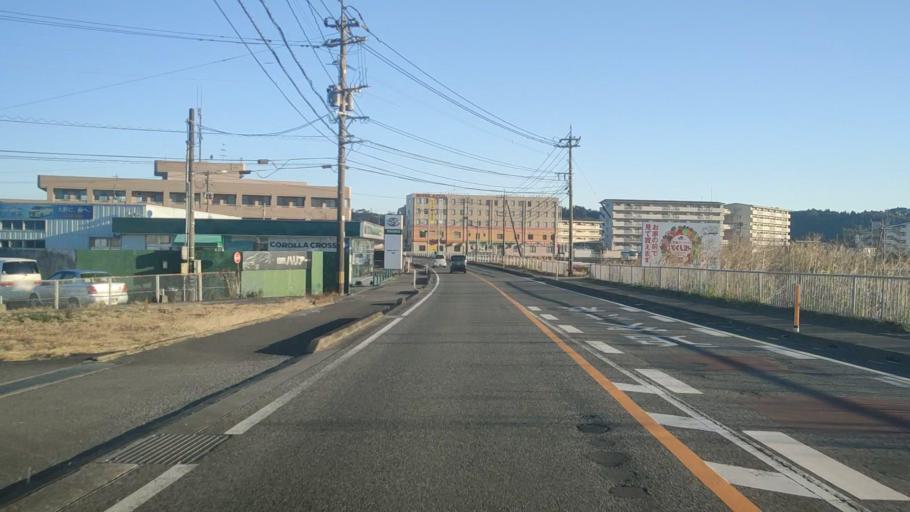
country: JP
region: Miyazaki
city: Takanabe
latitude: 32.1347
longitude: 131.5260
